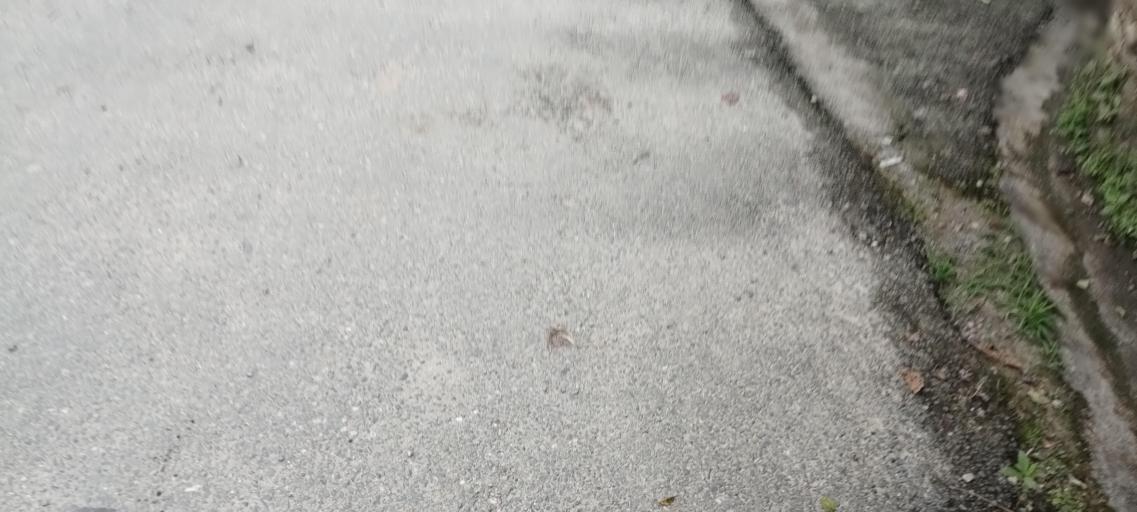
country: NP
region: Central Region
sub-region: Bagmati Zone
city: Kathmandu
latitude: 27.7829
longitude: 85.3629
